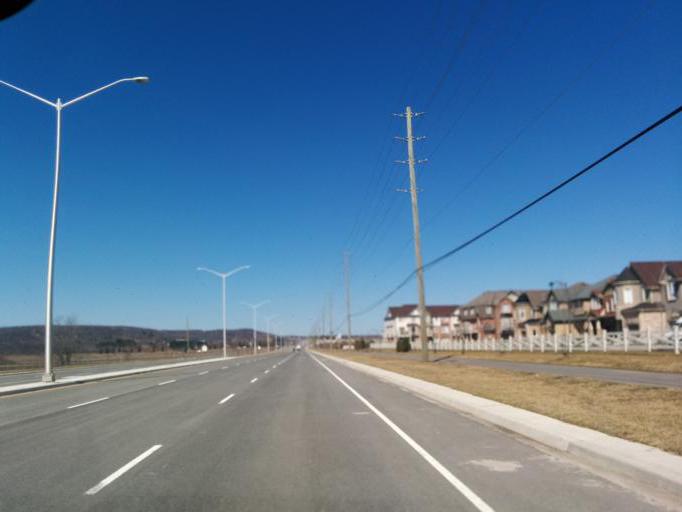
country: CA
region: Ontario
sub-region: Halton
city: Milton
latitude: 43.4795
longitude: -79.8745
